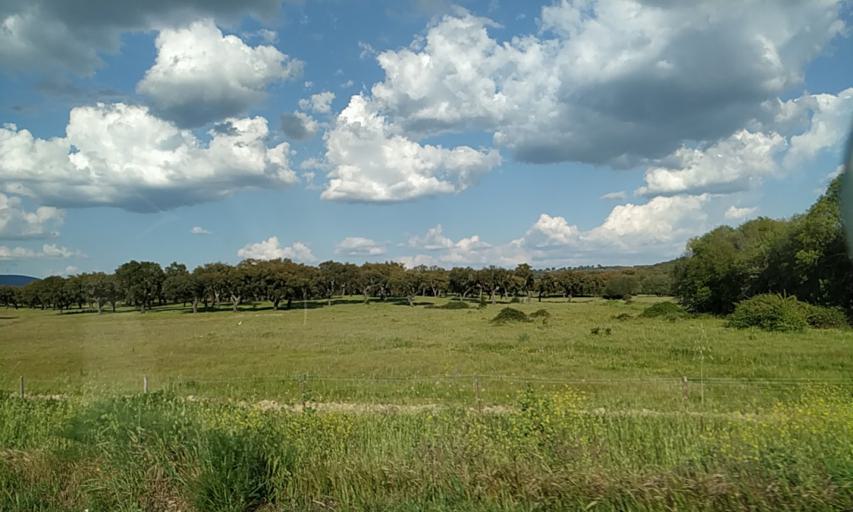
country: PT
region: Portalegre
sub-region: Portalegre
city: Urra
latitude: 39.2301
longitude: -7.4545
